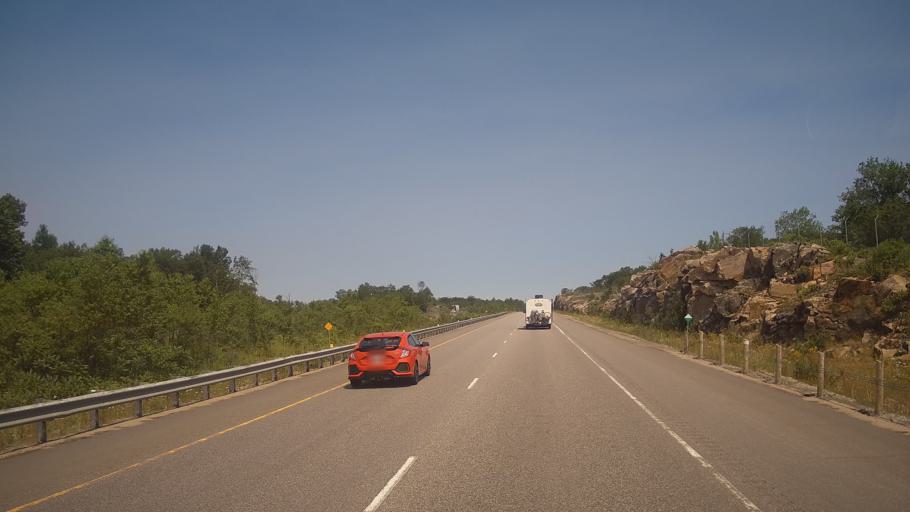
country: CA
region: Ontario
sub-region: Parry Sound District
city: Parry Sound
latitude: 45.1322
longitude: -79.7921
